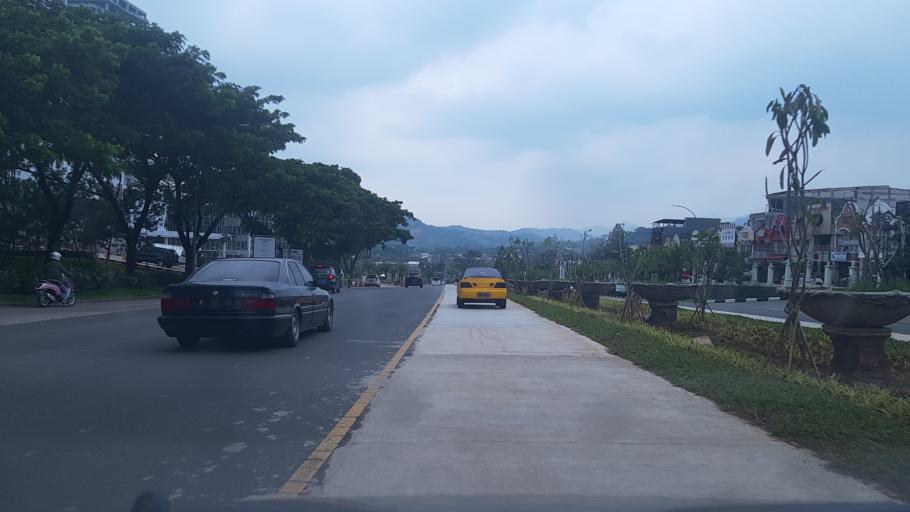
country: ID
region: West Java
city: Bogor
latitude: -6.5682
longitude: 106.8555
